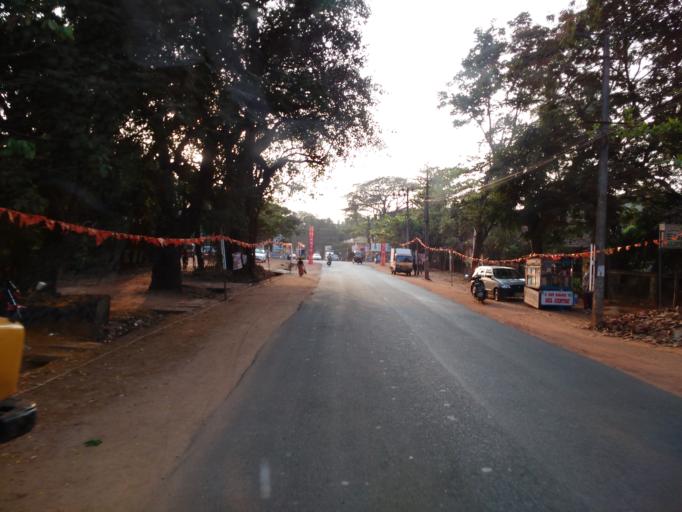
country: IN
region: Karnataka
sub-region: Dakshina Kannada
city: Mangalore
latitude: 12.8853
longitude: 74.8810
